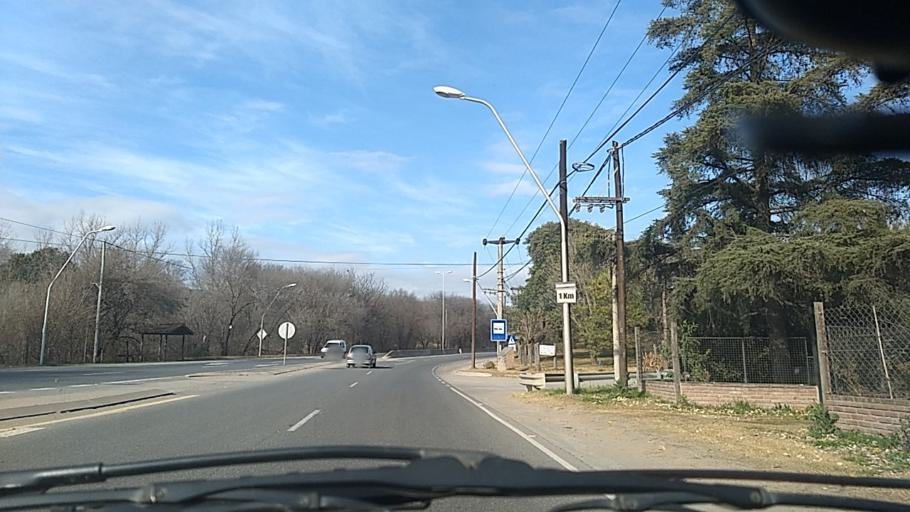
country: AR
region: Cordoba
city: Salsipuedes
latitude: -31.1537
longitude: -64.2993
